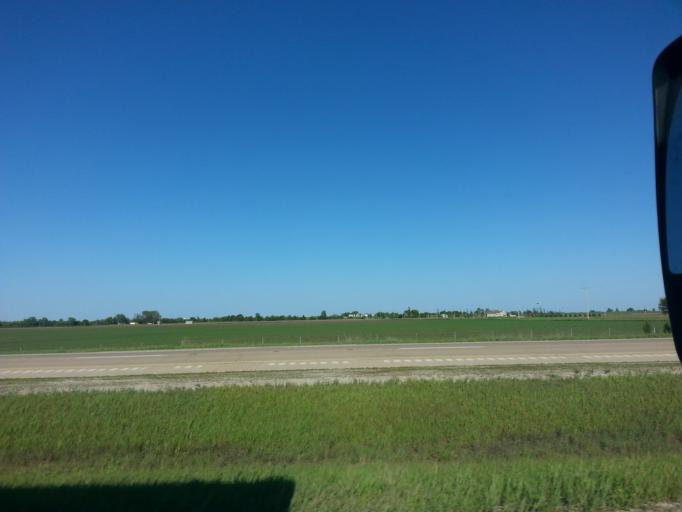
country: US
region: Illinois
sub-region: Woodford County
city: Minonk
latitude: 40.9704
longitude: -89.0565
